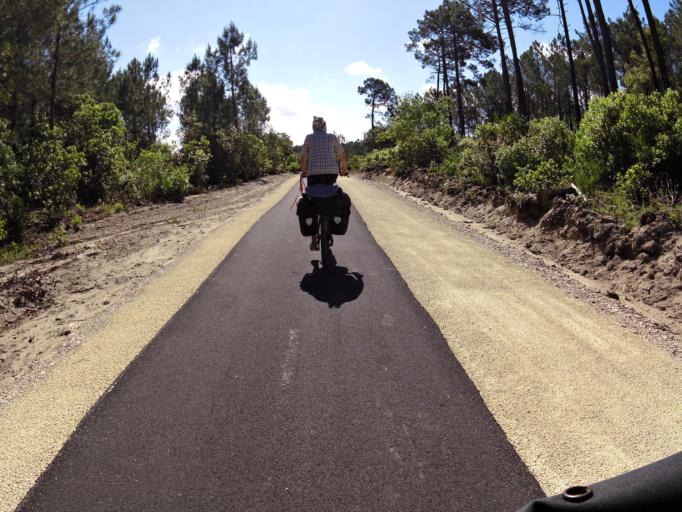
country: FR
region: Aquitaine
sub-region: Departement de la Gironde
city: Lacanau
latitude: 45.0290
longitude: -1.1719
